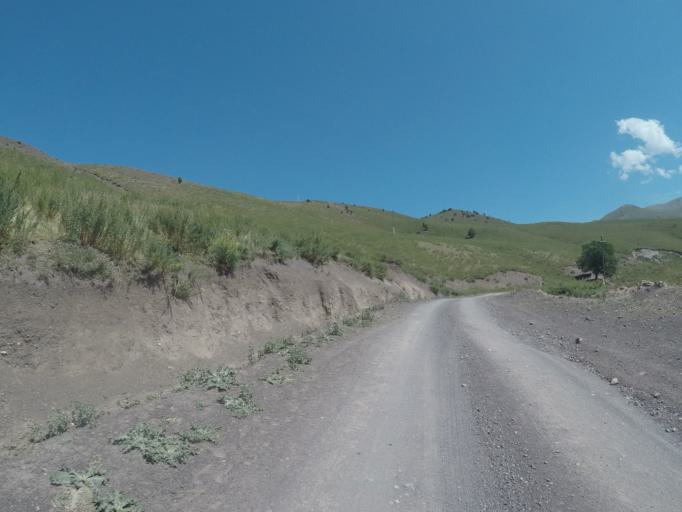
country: KG
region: Chuy
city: Bishkek
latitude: 42.6512
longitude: 74.5189
